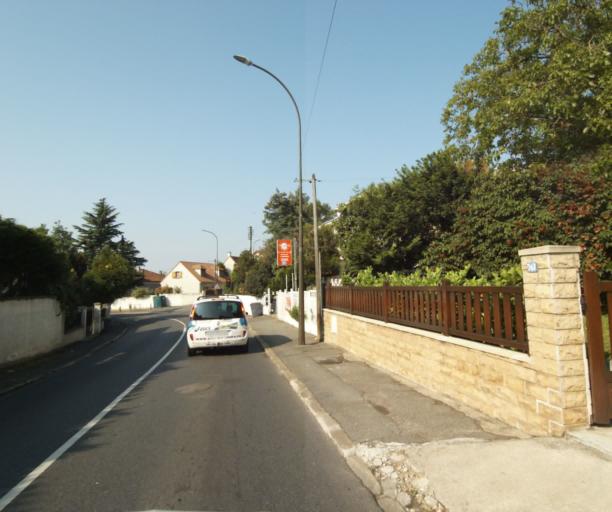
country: FR
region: Ile-de-France
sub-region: Departement du Val-d'Oise
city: Franconville
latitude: 48.9670
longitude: 2.2325
